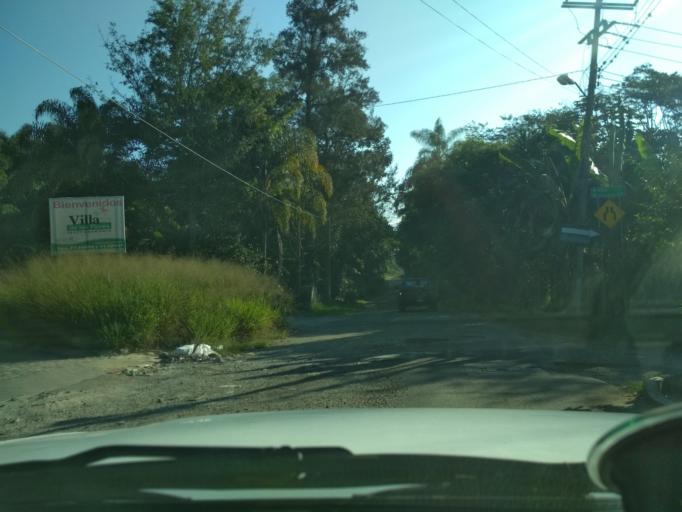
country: MX
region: Veracruz
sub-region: Fortin
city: Fraccionamiento Villas de la Llave
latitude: 18.9228
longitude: -96.9920
